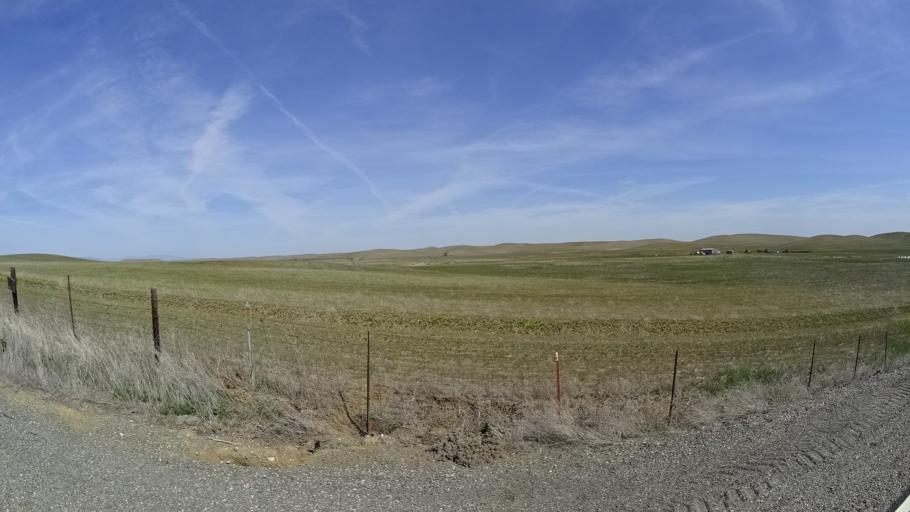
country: US
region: California
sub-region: Glenn County
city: Willows
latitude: 39.5315
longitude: -122.3173
